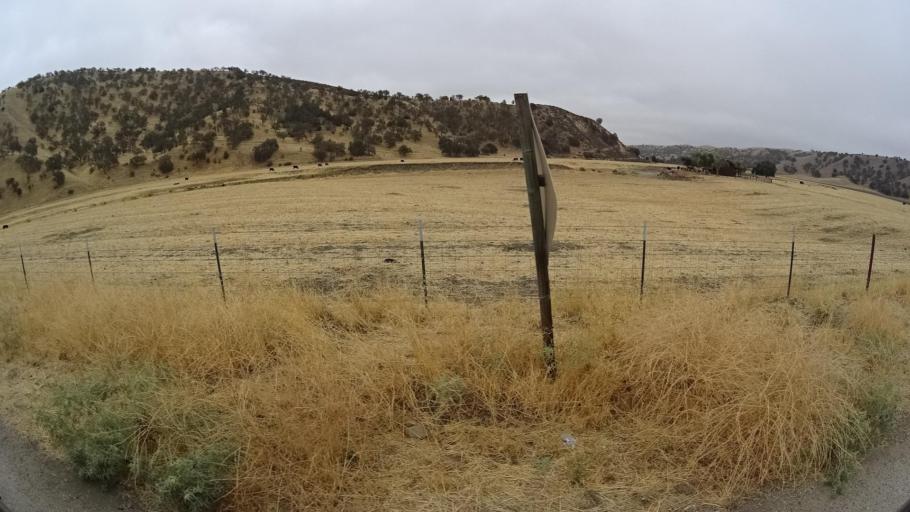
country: US
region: California
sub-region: San Luis Obispo County
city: San Miguel
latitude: 35.9077
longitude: -120.6949
